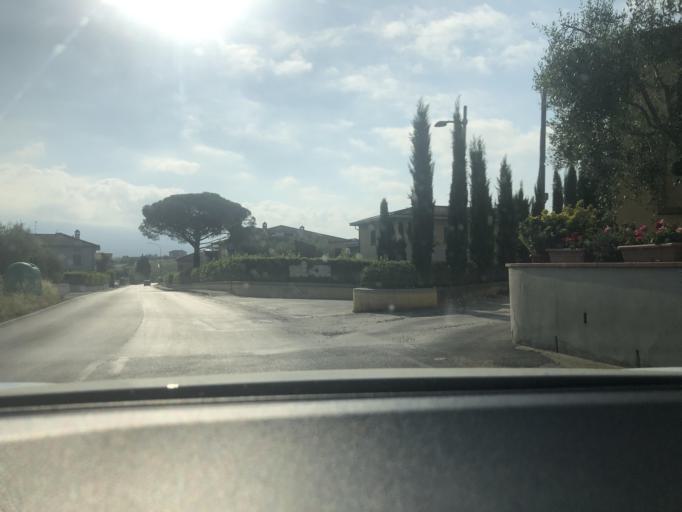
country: IT
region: Tuscany
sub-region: Provincia di Pistoia
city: Lamporecchio
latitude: 43.8060
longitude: 10.8706
